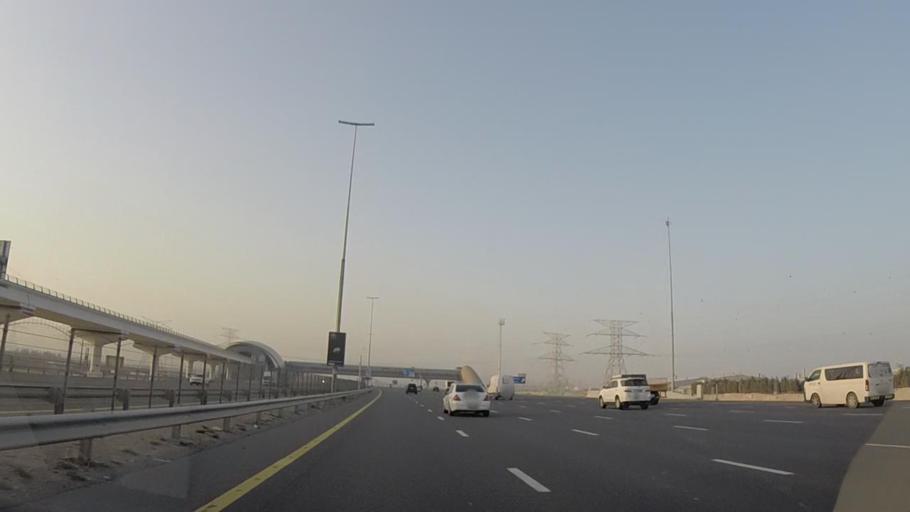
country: AE
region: Dubai
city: Dubai
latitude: 25.0290
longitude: 55.1020
